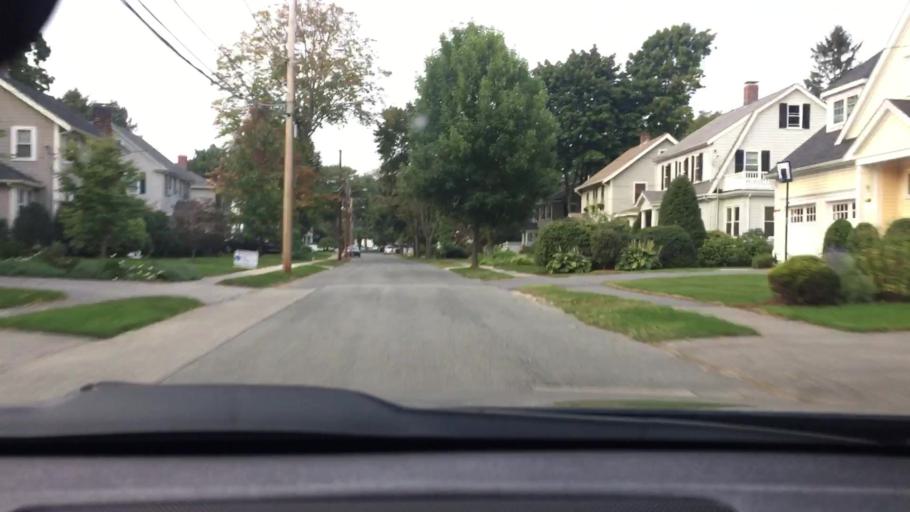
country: US
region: Massachusetts
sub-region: Norfolk County
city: Needham
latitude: 42.2783
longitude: -71.2250
